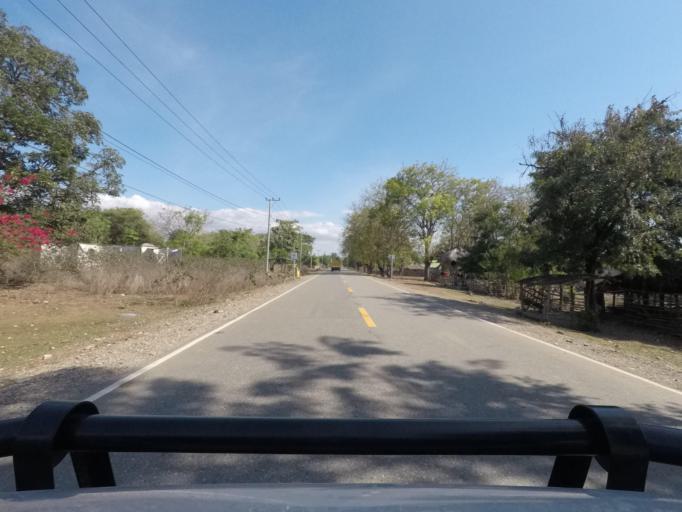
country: ID
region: East Nusa Tenggara
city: Atambua
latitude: -8.9212
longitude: 124.9926
